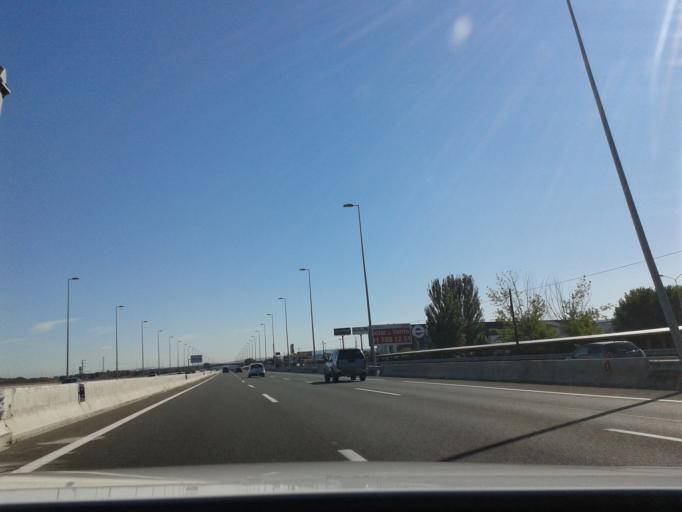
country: ES
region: Madrid
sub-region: Provincia de Madrid
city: Alcala de Henares
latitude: 40.5076
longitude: -3.3263
